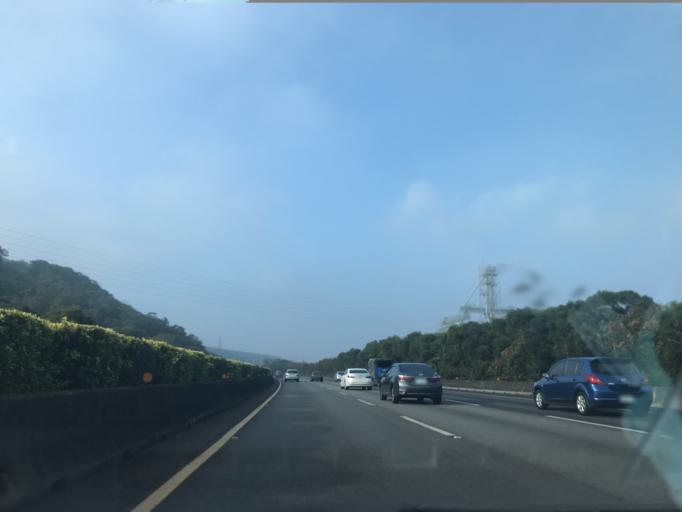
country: TW
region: Taiwan
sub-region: Hsinchu
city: Zhubei
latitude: 24.8824
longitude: 121.0745
